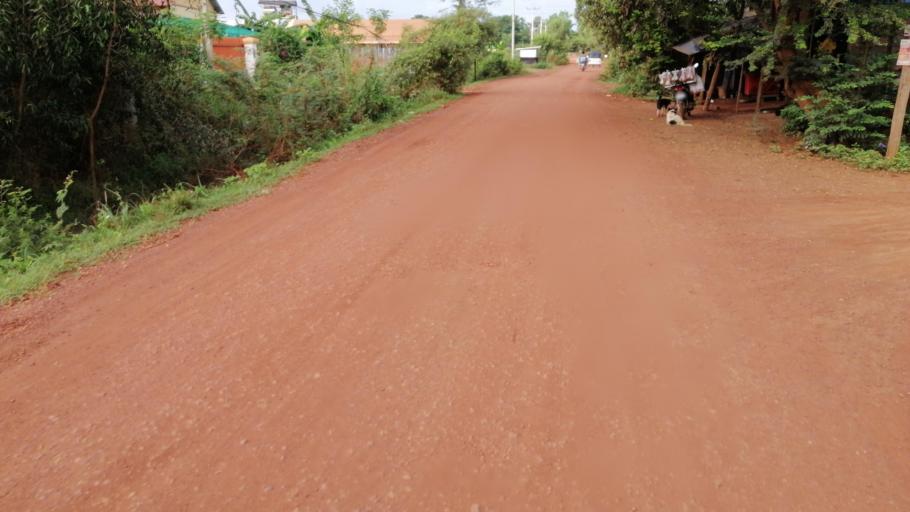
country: KH
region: Siem Reap
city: Siem Reap
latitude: 13.3607
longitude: 103.8296
